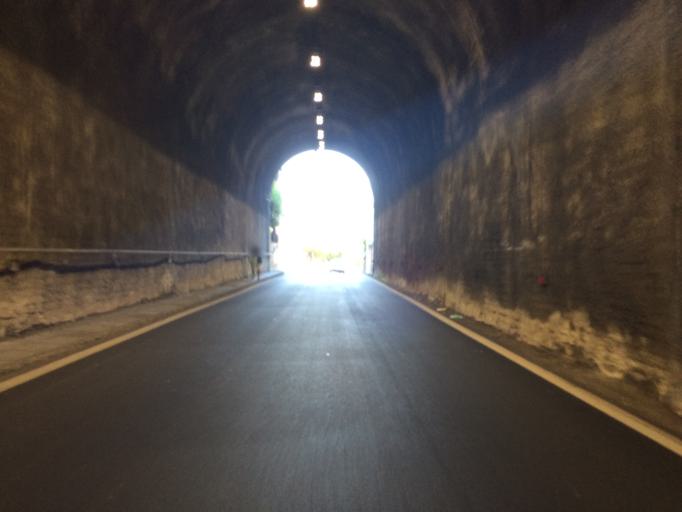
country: IT
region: Liguria
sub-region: Provincia di Genova
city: Camogli
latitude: 44.3436
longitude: 9.1719
